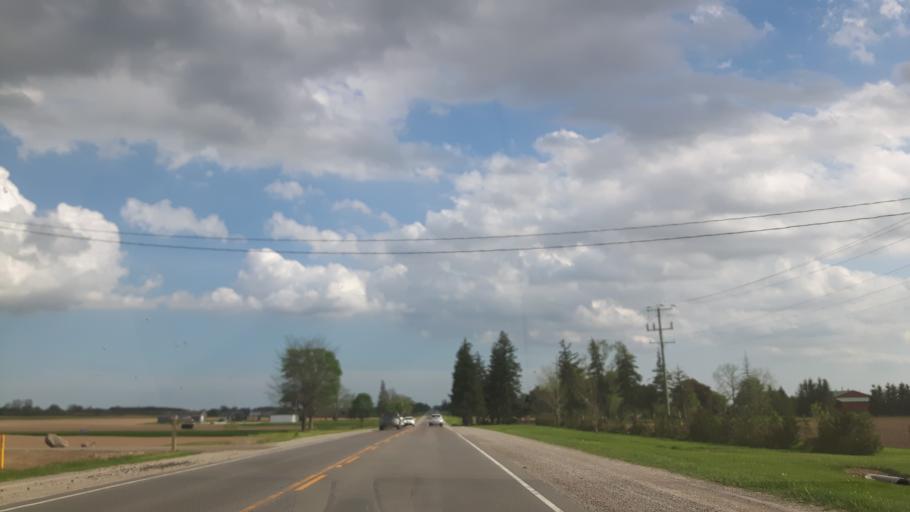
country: CA
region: Ontario
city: South Huron
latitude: 43.2325
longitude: -81.4578
